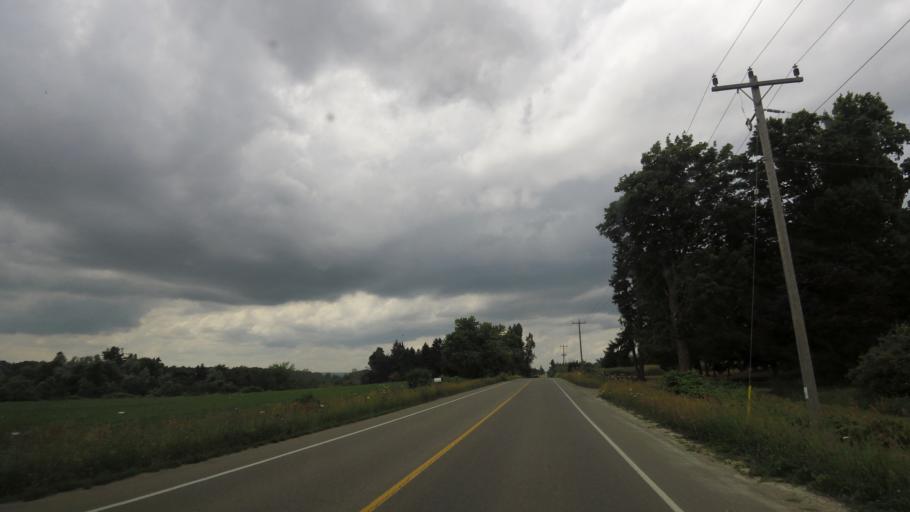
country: CA
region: Ontario
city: Brampton
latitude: 43.7614
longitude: -79.8386
